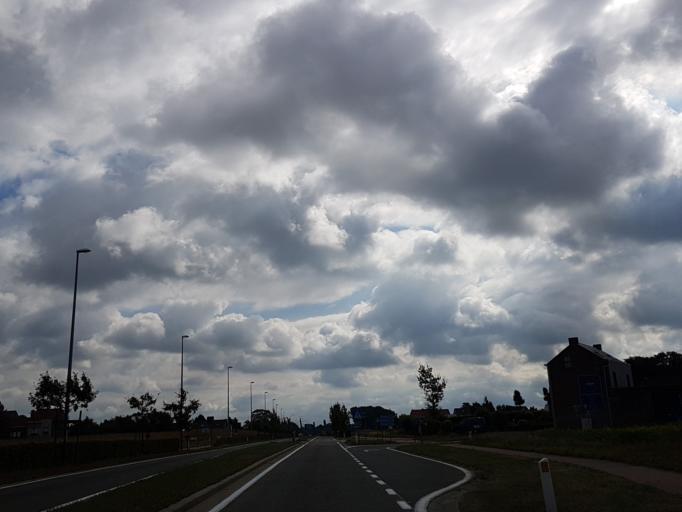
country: BE
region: Flanders
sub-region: Provincie Vlaams-Brabant
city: Tienen
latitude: 50.8014
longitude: 4.9199
